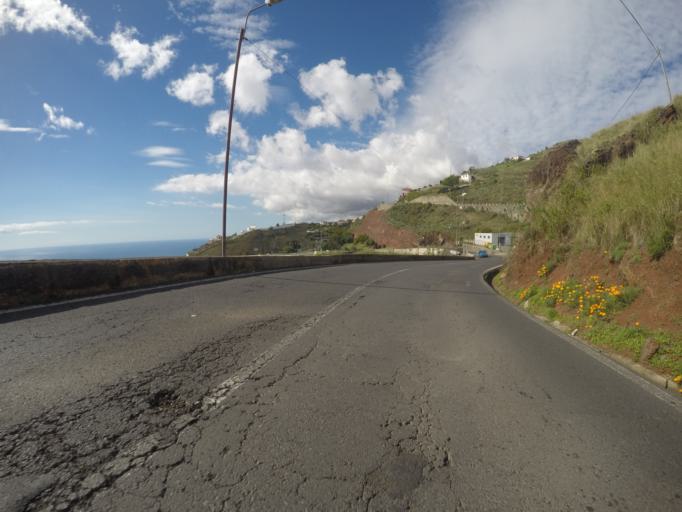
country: PT
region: Madeira
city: Canico
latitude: 32.6466
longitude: -16.8636
